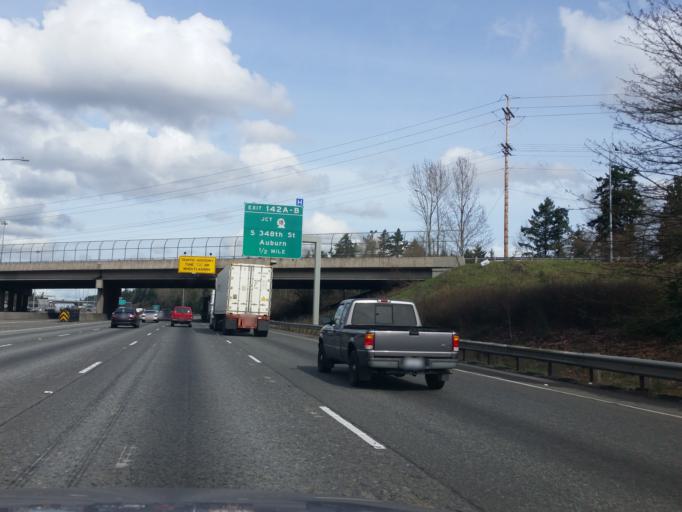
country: US
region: Washington
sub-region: King County
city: Lakeland South
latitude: 47.2779
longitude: -122.3112
